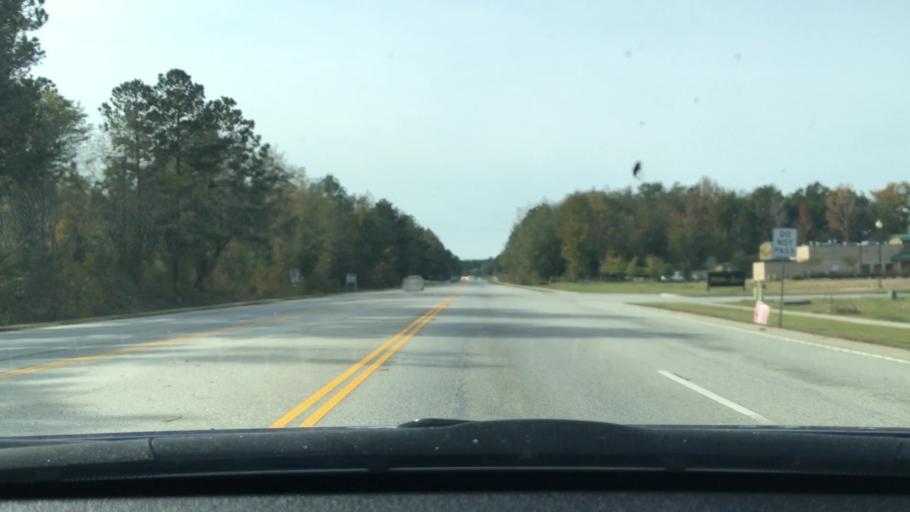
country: US
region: South Carolina
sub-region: Sumter County
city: Cherryvale
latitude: 33.9374
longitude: -80.4232
